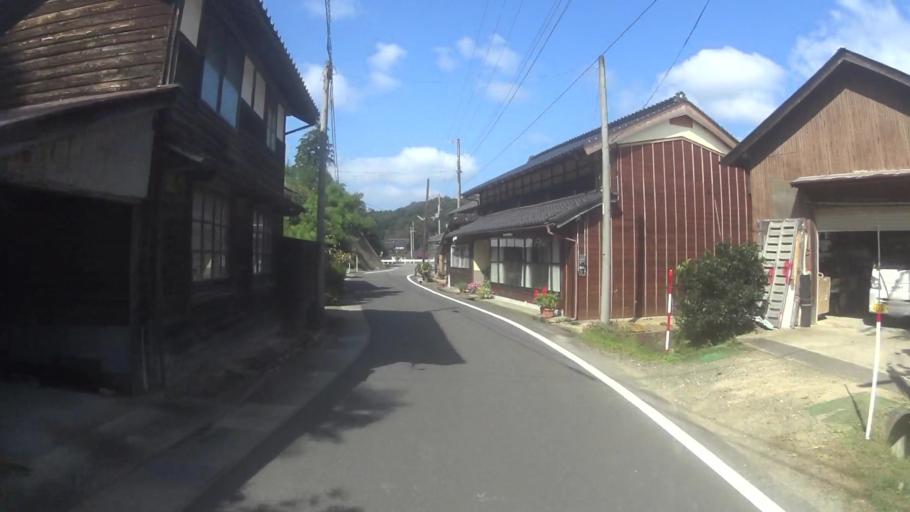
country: JP
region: Kyoto
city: Miyazu
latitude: 35.7121
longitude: 135.1152
